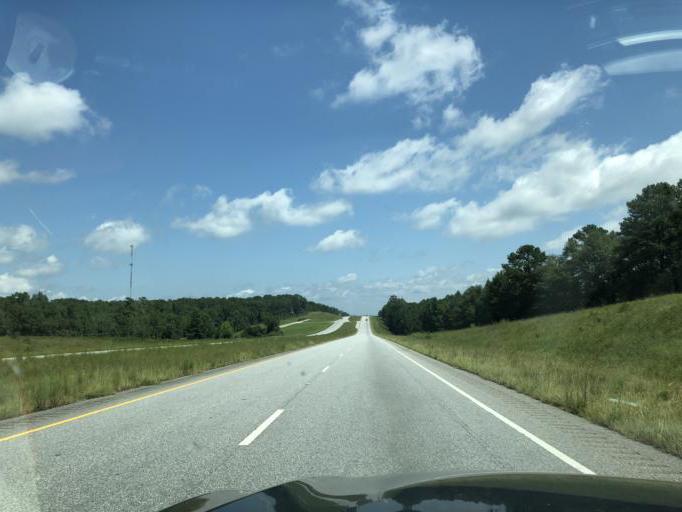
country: US
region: Alabama
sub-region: Barbour County
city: Eufaula
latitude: 31.7620
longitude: -85.2026
